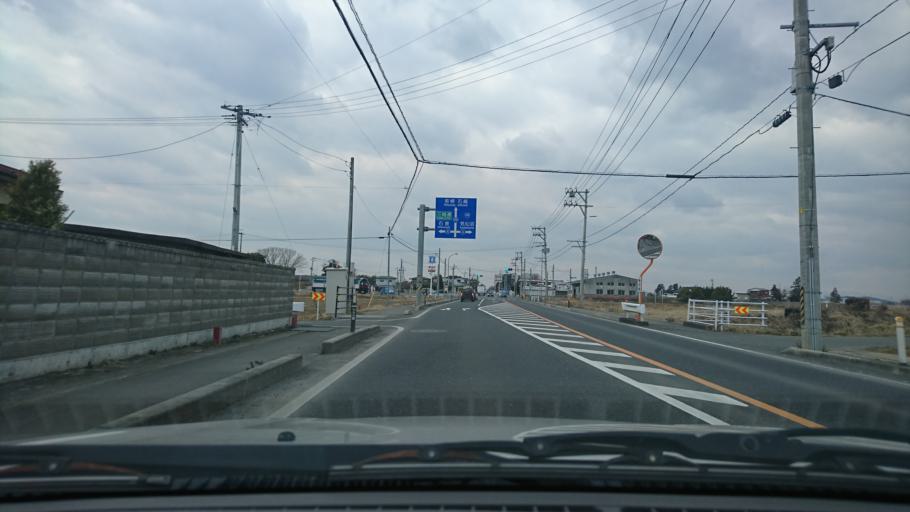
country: JP
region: Miyagi
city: Wakuya
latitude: 38.7078
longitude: 141.2613
